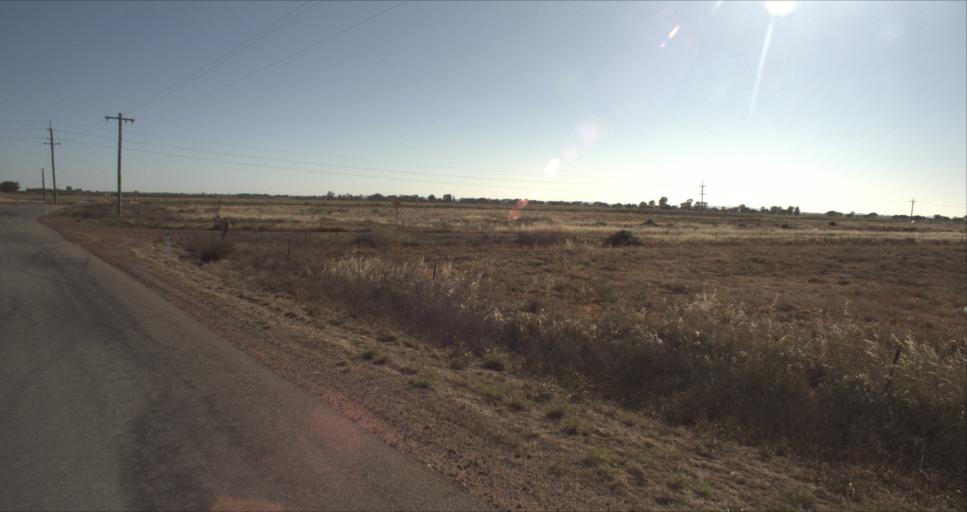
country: AU
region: New South Wales
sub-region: Leeton
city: Leeton
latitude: -34.5507
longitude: 146.2674
